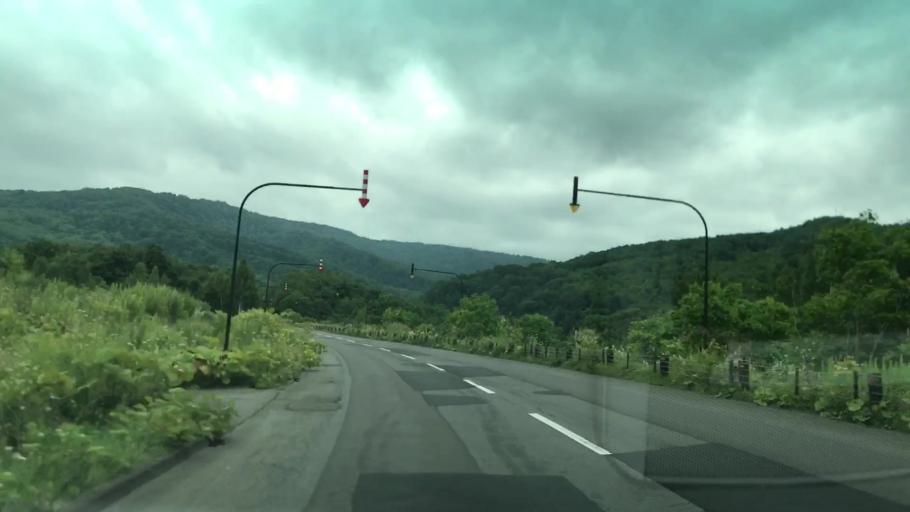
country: JP
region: Hokkaido
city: Yoichi
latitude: 43.0107
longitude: 140.8696
